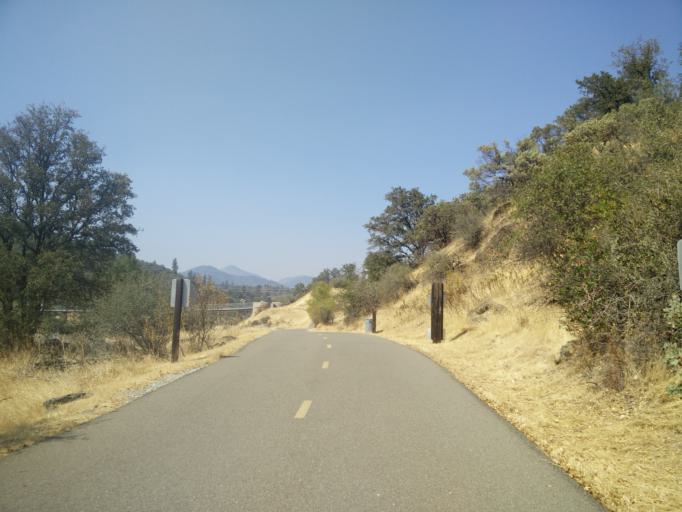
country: US
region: California
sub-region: Shasta County
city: Shasta
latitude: 40.6006
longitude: -122.4423
